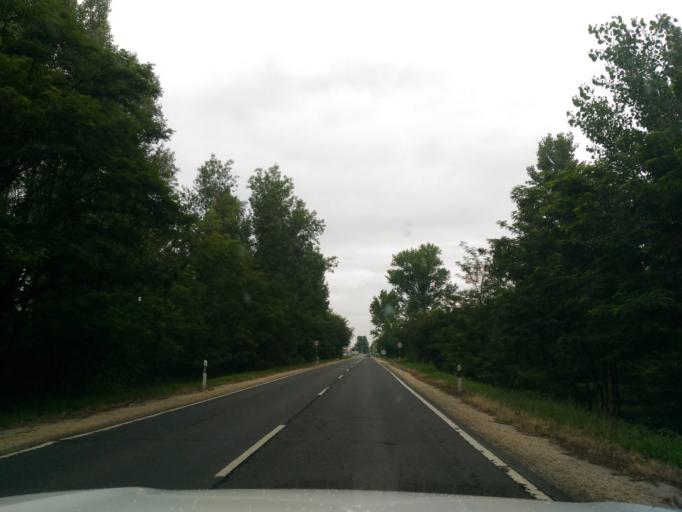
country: HU
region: Pest
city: Alsonemedi
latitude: 47.2984
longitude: 19.1825
